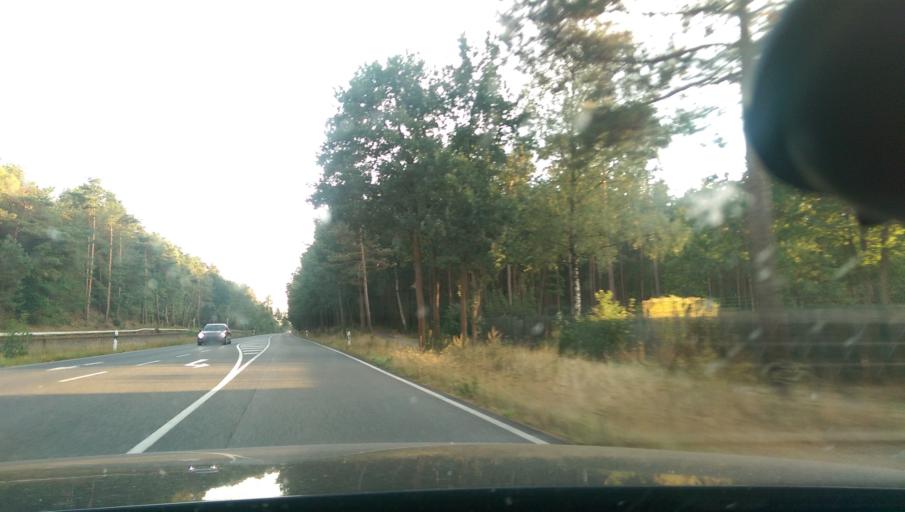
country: DE
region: Lower Saxony
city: Walsrode
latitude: 52.8237
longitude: 9.5937
